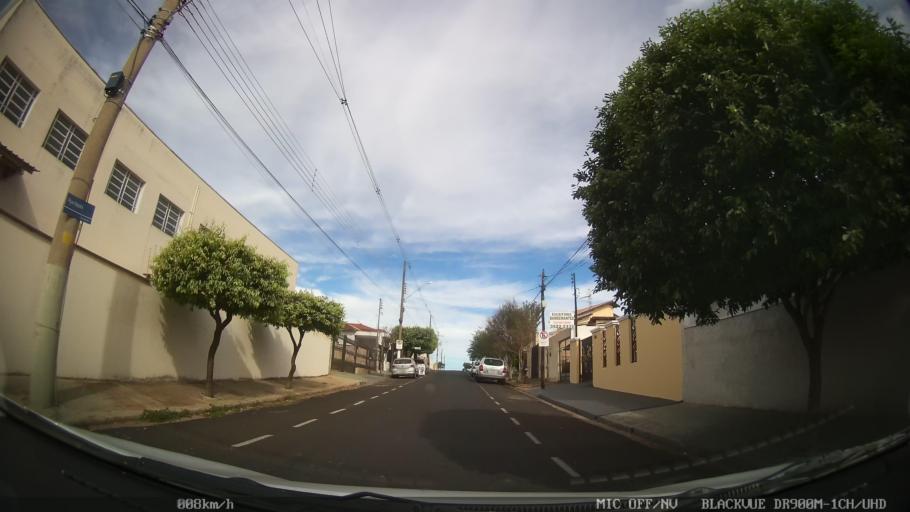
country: BR
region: Sao Paulo
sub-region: Catanduva
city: Catanduva
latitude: -21.1460
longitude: -48.9836
